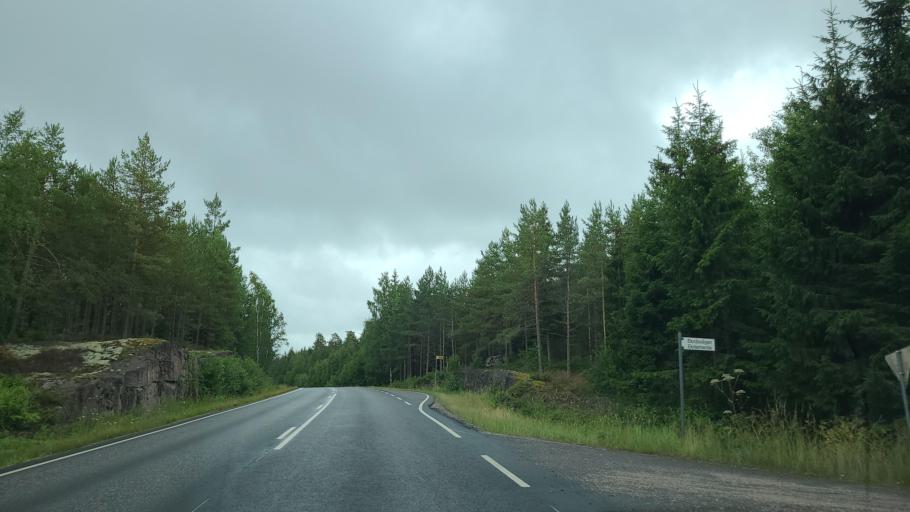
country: FI
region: Varsinais-Suomi
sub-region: Aboland-Turunmaa
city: Kimito
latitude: 60.2111
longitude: 22.6396
